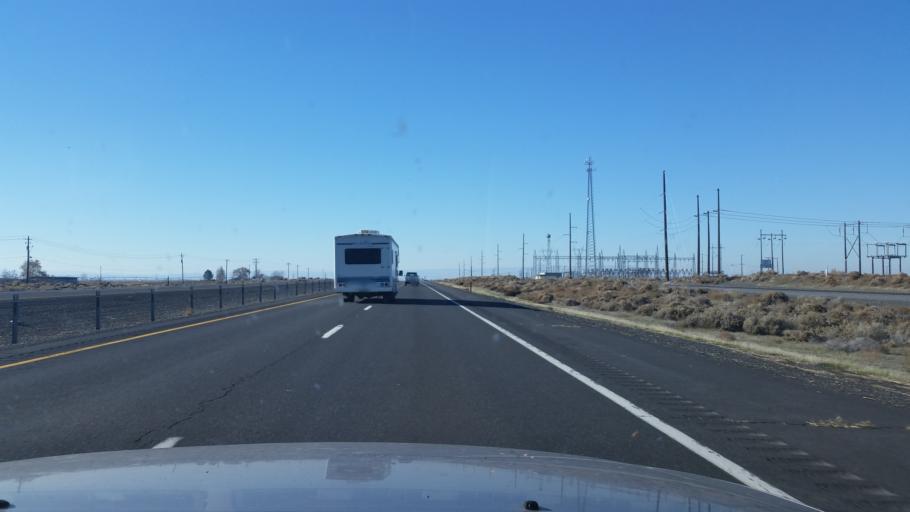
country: US
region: Washington
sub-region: Grant County
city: Cascade Valley
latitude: 47.1041
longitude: -119.5225
